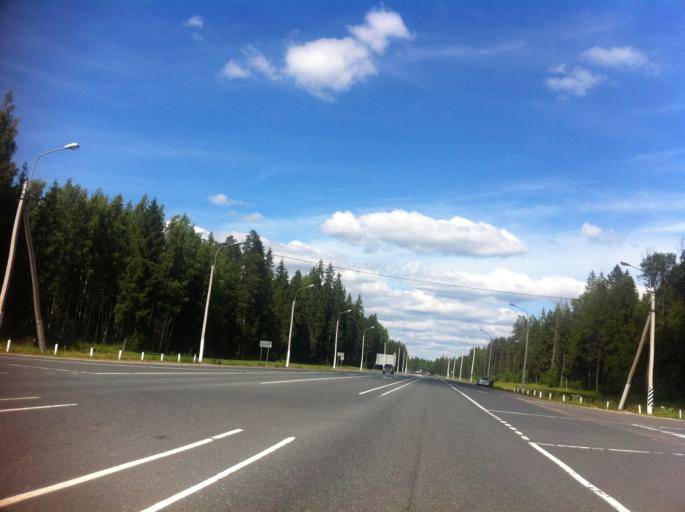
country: RU
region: Leningrad
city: Luga
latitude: 58.6353
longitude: 29.8445
